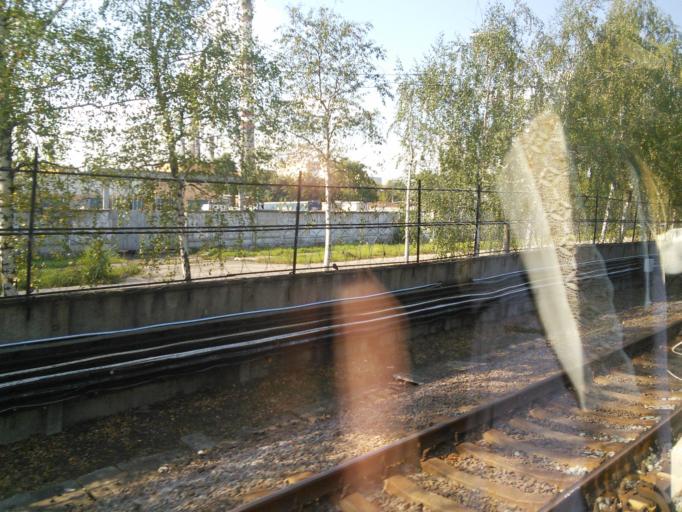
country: RU
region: Moskovskaya
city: Kozhukhovo
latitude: 55.6978
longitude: 37.6621
